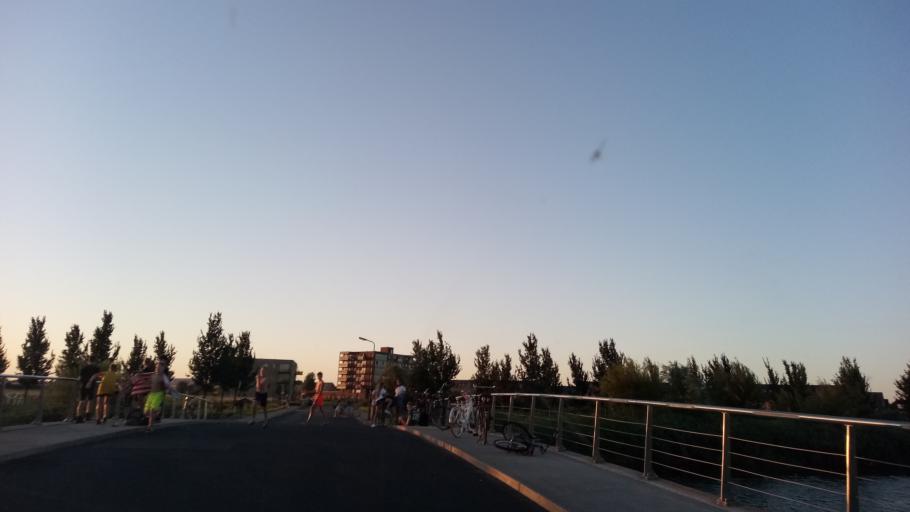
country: NL
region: North Holland
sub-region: Gemeente Langedijk
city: Broek op Langedijk
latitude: 52.6501
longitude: 4.8053
